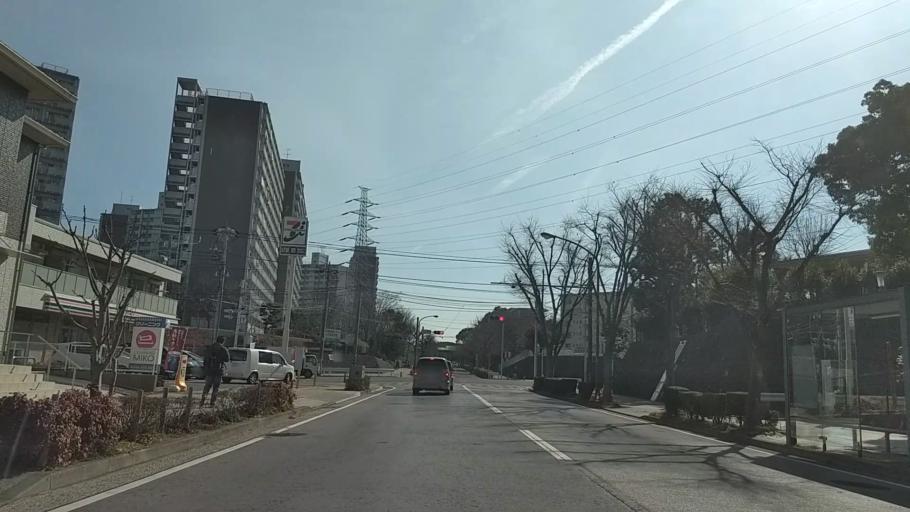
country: JP
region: Kanagawa
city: Kamakura
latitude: 35.3738
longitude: 139.5814
